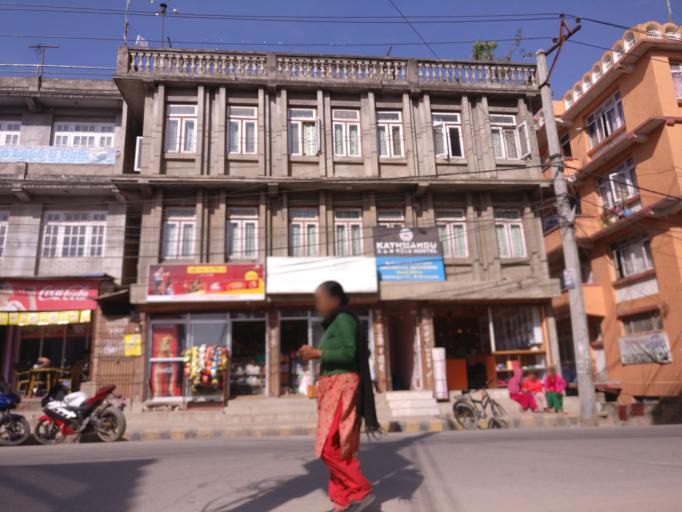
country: NP
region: Central Region
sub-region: Bagmati Zone
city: Patan
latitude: 27.6716
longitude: 85.3385
